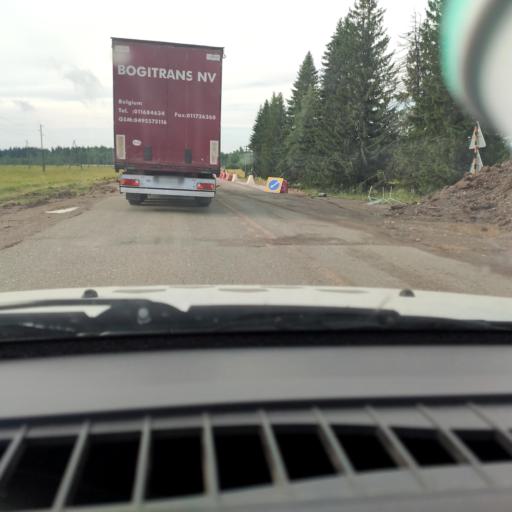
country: RU
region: Kirov
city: Kostino
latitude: 58.8256
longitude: 53.3100
